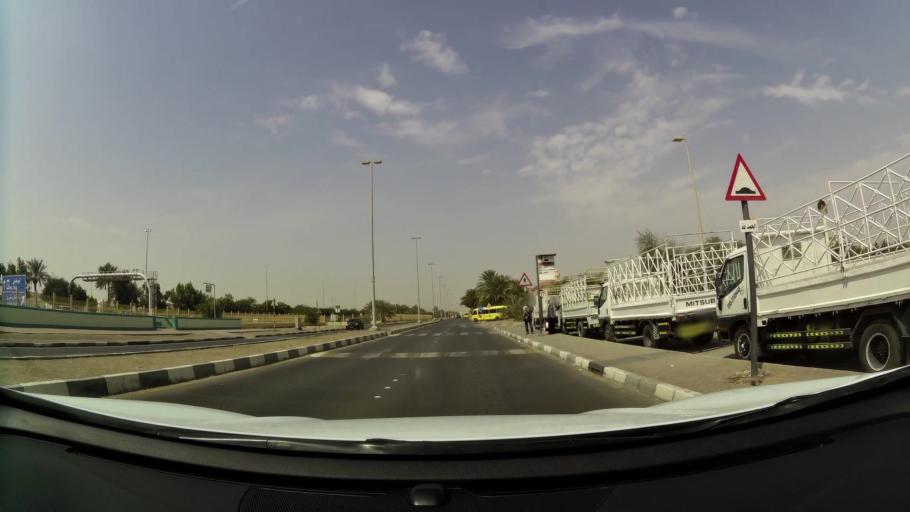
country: AE
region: Abu Dhabi
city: Abu Dhabi
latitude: 24.2936
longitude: 54.6324
